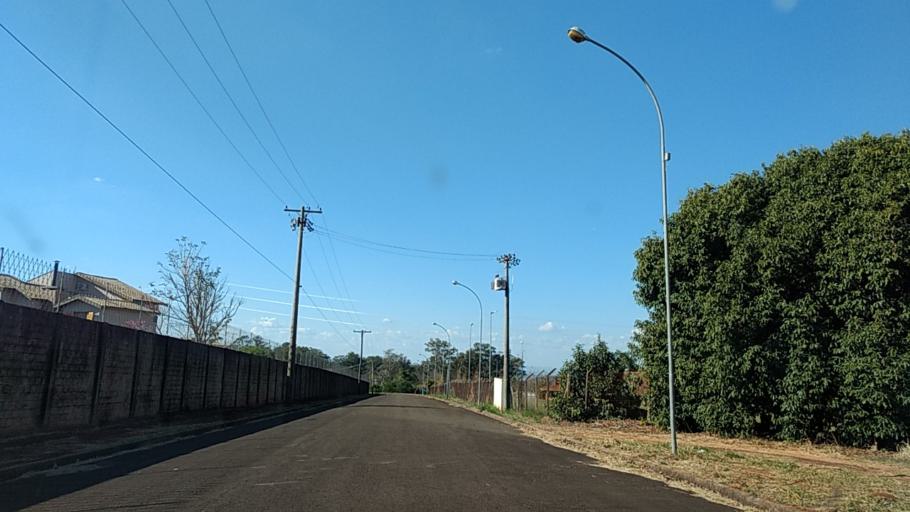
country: BR
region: Sao Paulo
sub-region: Botucatu
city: Botucatu
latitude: -22.8537
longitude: -48.4361
